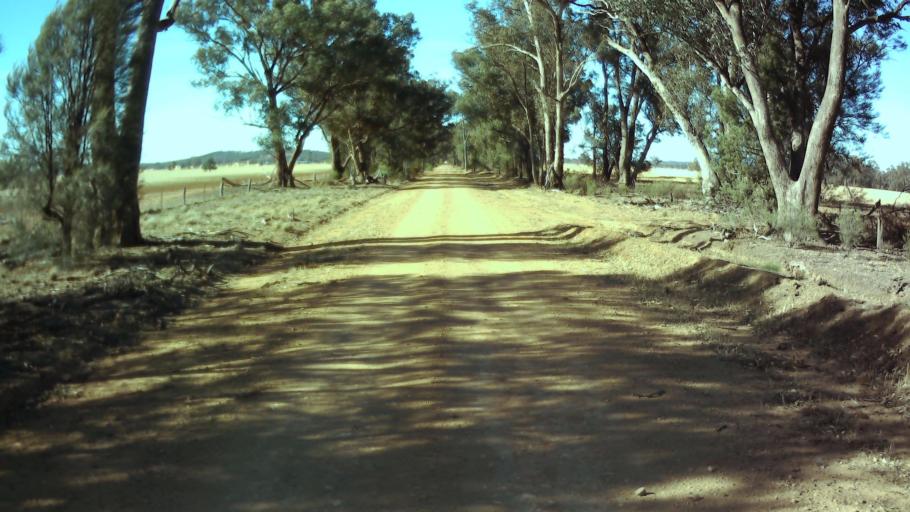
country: AU
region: New South Wales
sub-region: Weddin
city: Grenfell
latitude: -33.8285
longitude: 147.8740
